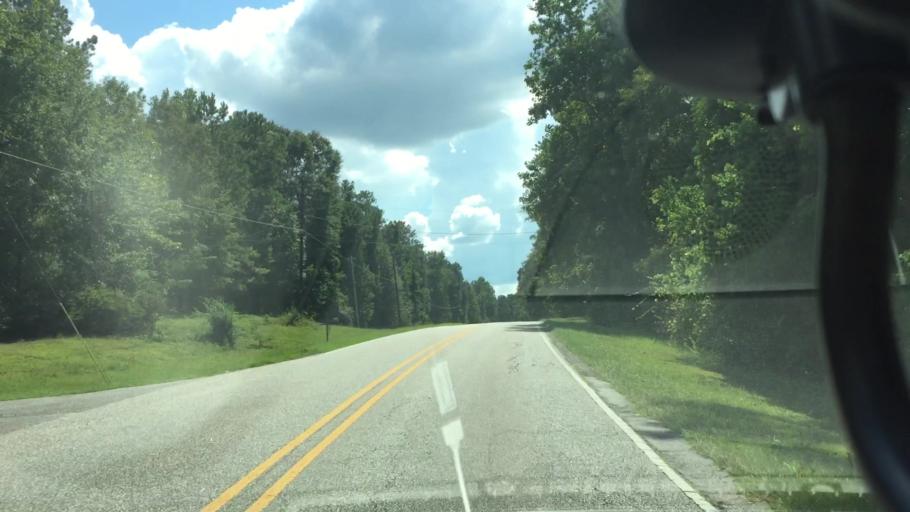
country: US
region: Alabama
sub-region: Lee County
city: Auburn
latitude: 32.5613
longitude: -85.5249
